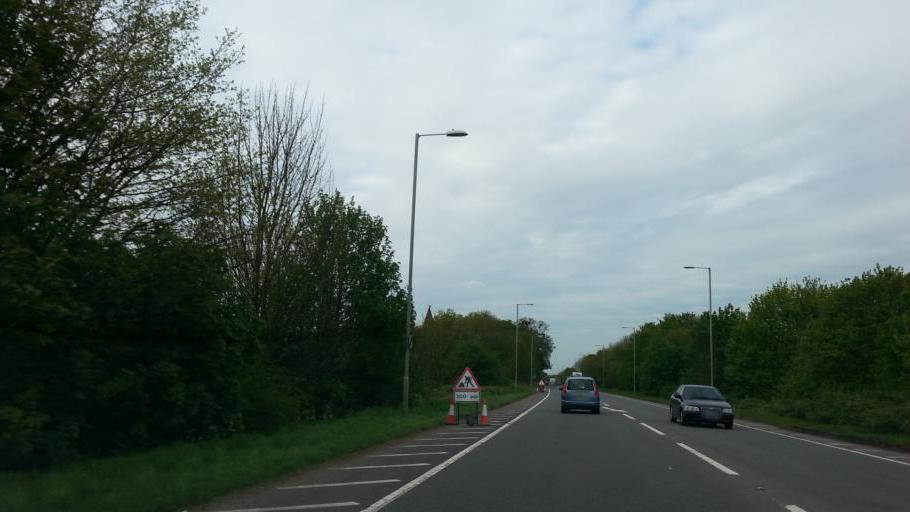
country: GB
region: England
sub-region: Cambridgeshire
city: Doddington
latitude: 52.5054
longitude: 0.0840
